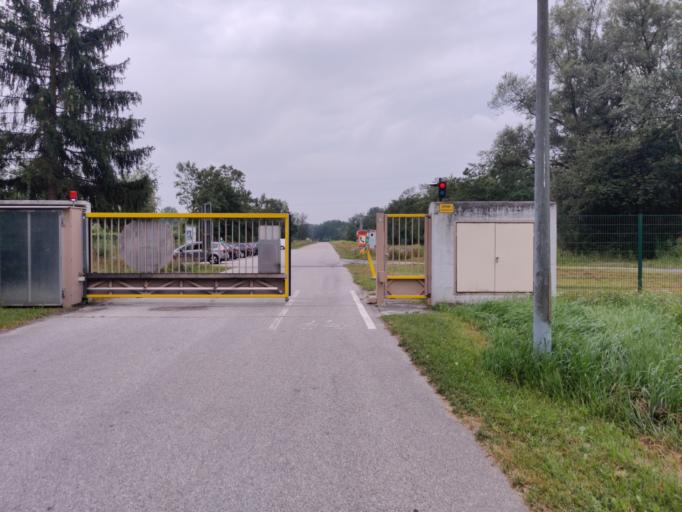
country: AT
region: Upper Austria
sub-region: Politischer Bezirk Linz-Land
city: Asten
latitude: 48.2450
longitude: 14.4279
